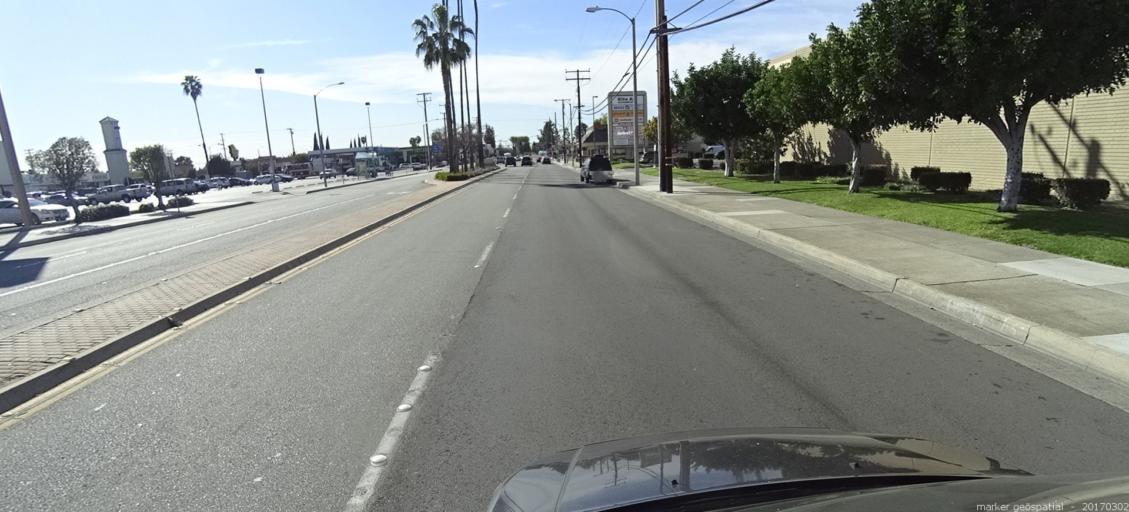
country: US
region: California
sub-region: Orange County
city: Cypress
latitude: 33.8320
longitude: -118.0090
